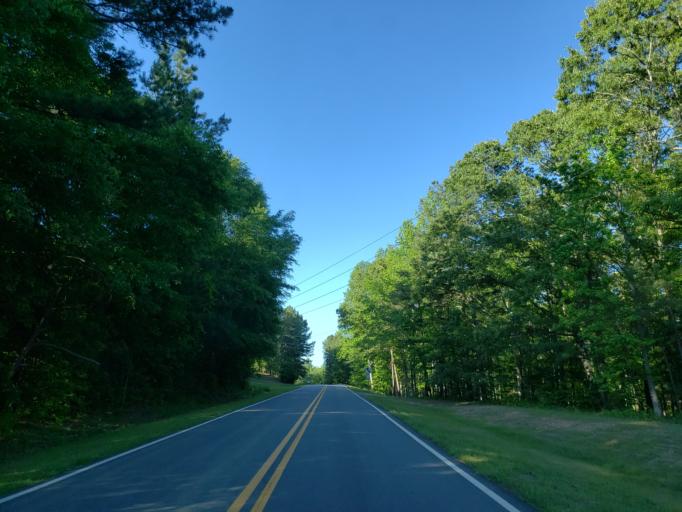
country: US
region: Georgia
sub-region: Haralson County
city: Buchanan
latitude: 33.8011
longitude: -85.2397
